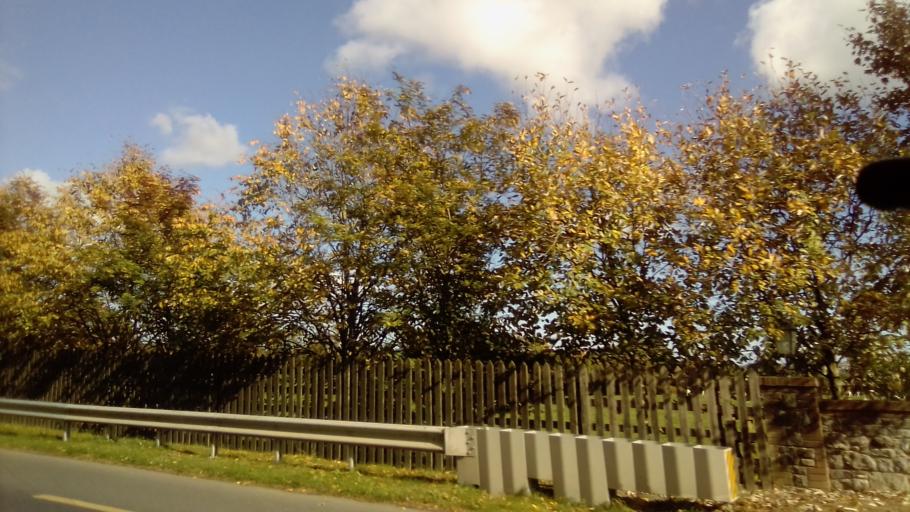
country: IE
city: Kentstown
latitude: 53.6176
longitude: -6.4821
